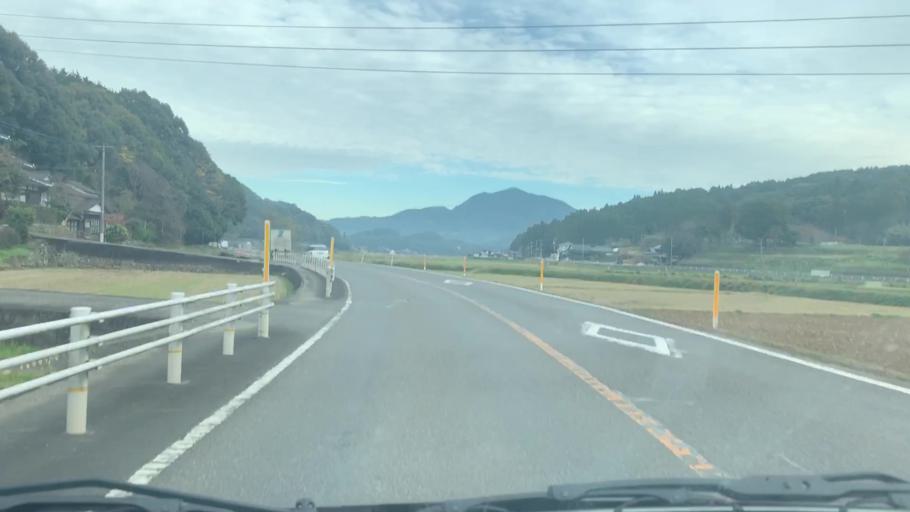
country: JP
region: Saga Prefecture
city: Takeocho-takeo
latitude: 33.2326
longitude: 129.9667
